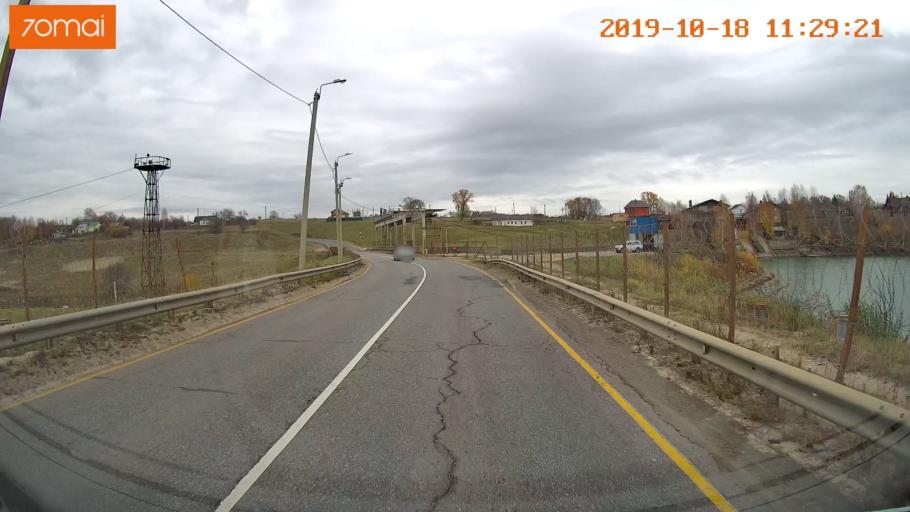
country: RU
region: Rjazan
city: Oktyabr'skiy
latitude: 54.1566
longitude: 38.6761
